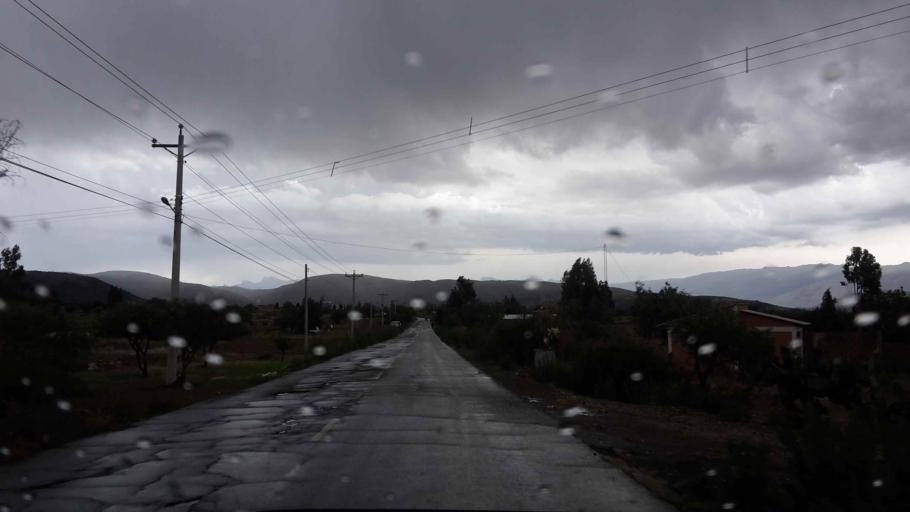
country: BO
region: Cochabamba
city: Tarata
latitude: -17.5647
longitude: -66.0786
